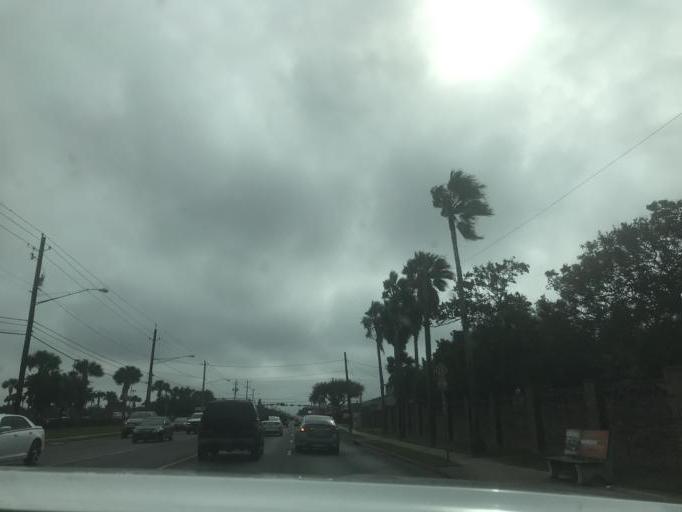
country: US
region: Texas
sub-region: Nueces County
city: Corpus Christi
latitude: 27.7023
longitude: -97.3629
